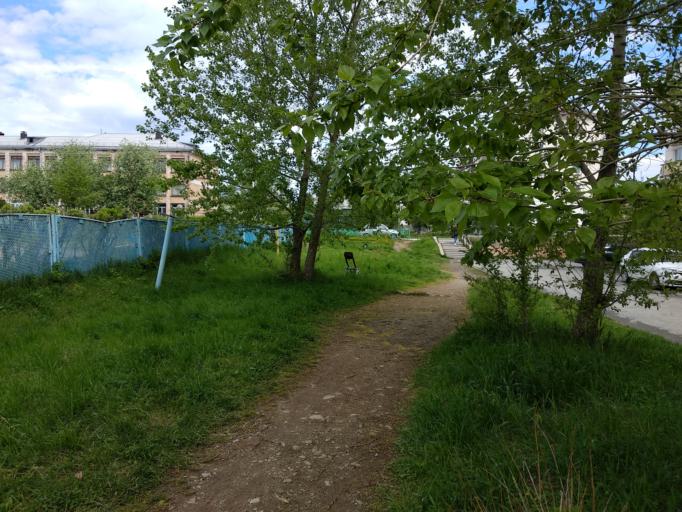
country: RU
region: Sverdlovsk
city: Krasnotur'insk
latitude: 59.7614
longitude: 60.1918
